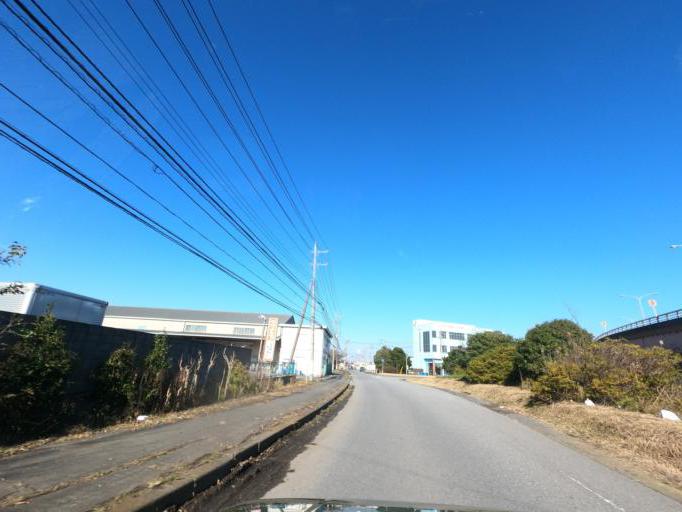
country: JP
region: Ibaraki
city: Mitsukaido
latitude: 35.9989
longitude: 139.9793
